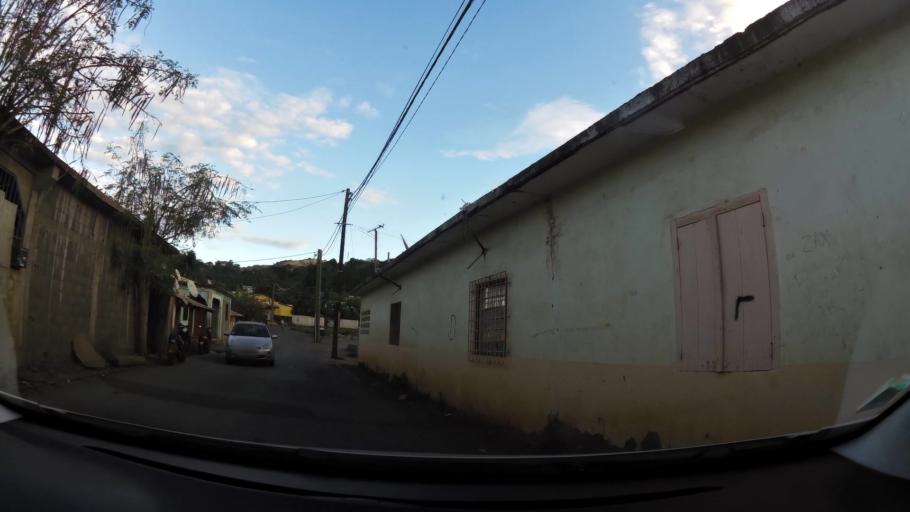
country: YT
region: Koungou
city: Koungou
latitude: -12.7302
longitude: 45.1869
